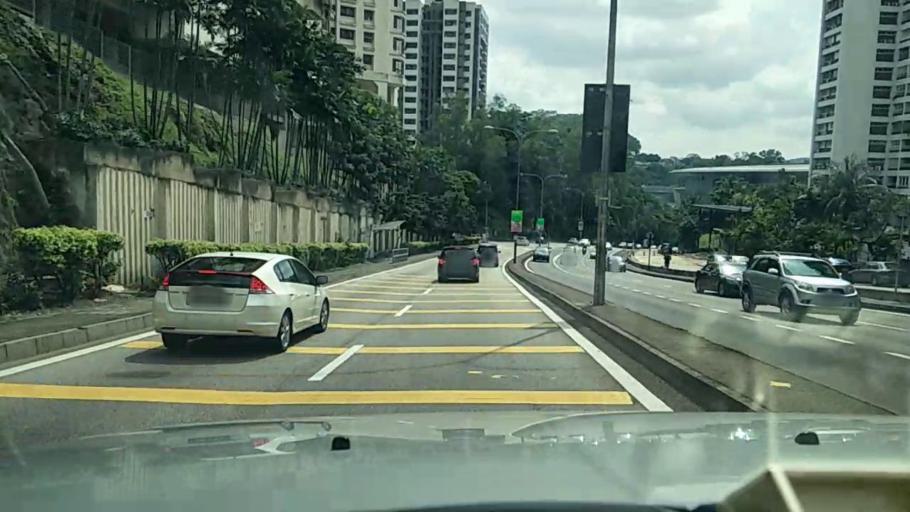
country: MY
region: Kuala Lumpur
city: Kuala Lumpur
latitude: 3.1423
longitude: 101.6653
